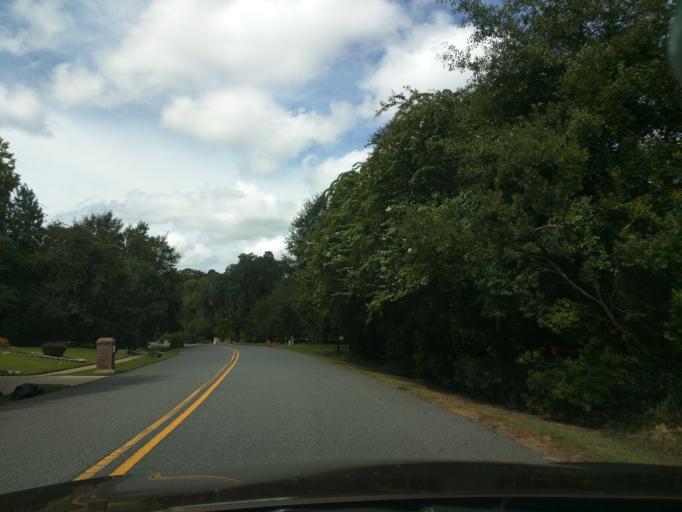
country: US
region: Florida
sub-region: Leon County
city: Tallahassee
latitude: 30.5730
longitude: -84.2618
